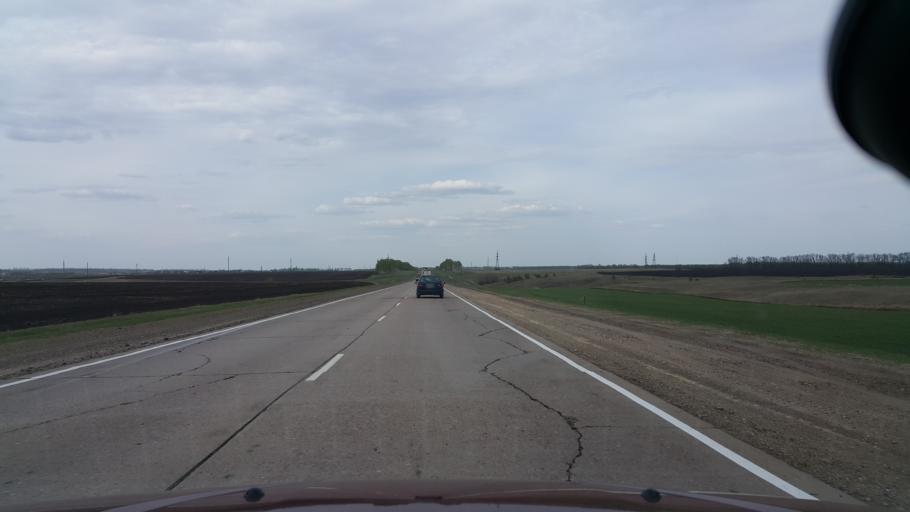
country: RU
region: Tambov
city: Pokrovo-Prigorodnoye
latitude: 52.6279
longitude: 41.3426
